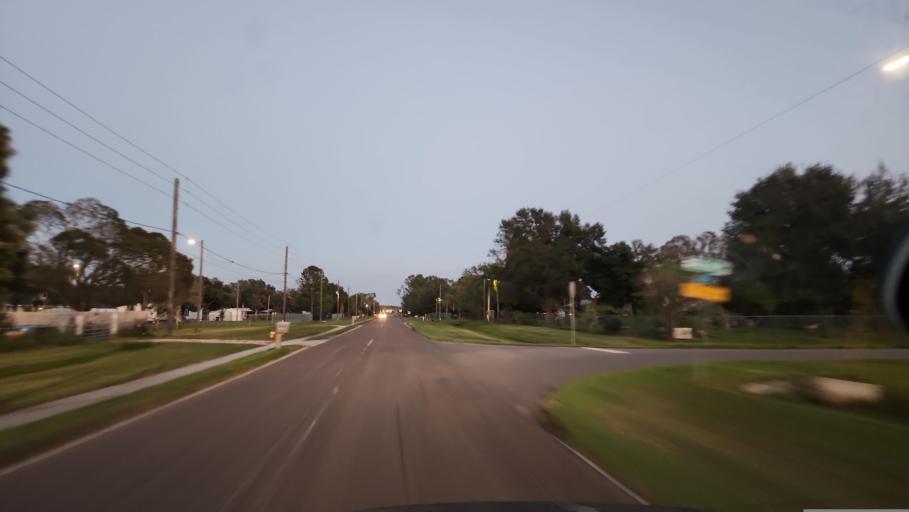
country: US
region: Florida
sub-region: Hillsborough County
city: Balm
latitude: 27.8013
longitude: -82.2797
